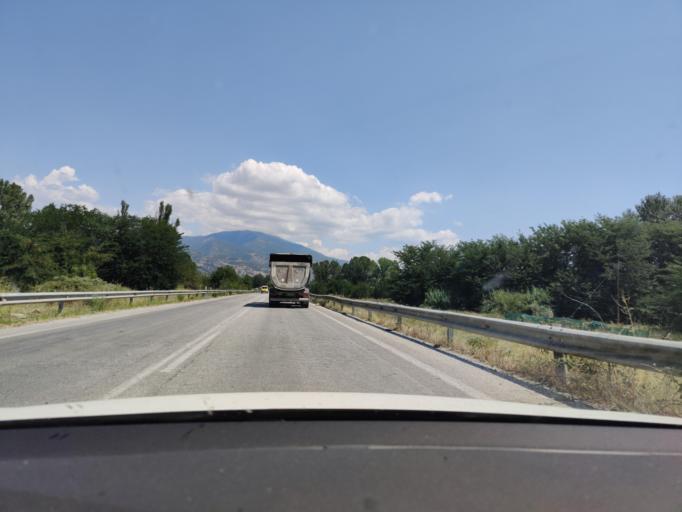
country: GR
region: Central Macedonia
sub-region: Nomos Serron
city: Serres
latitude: 41.0764
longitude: 23.5662
